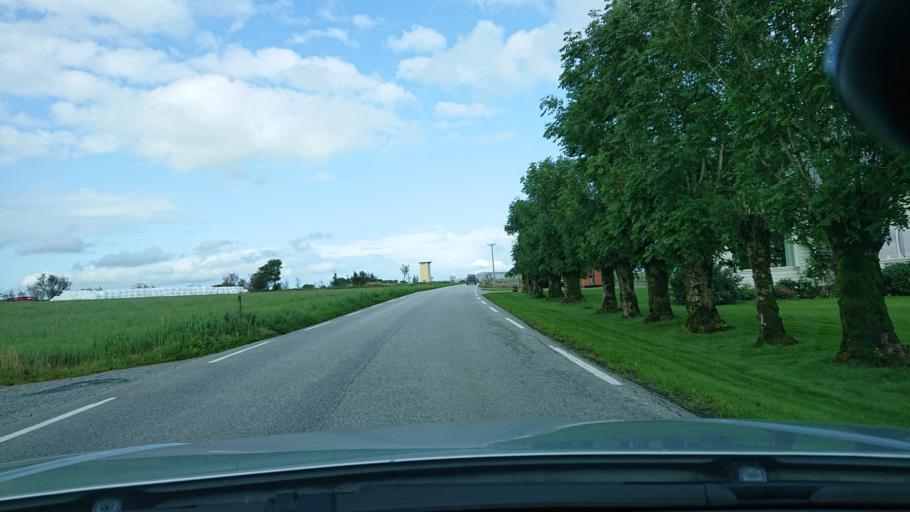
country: NO
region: Rogaland
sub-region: Gjesdal
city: Algard
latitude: 58.6914
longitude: 5.7704
